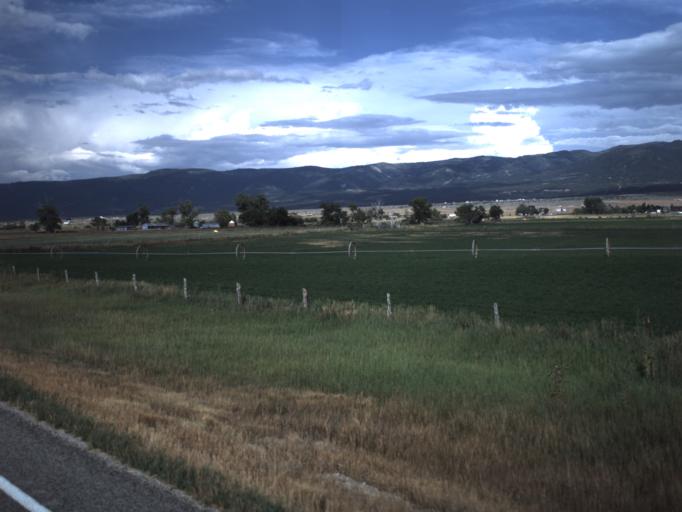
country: US
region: Utah
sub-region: Sanpete County
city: Mount Pleasant
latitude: 39.4983
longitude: -111.5067
